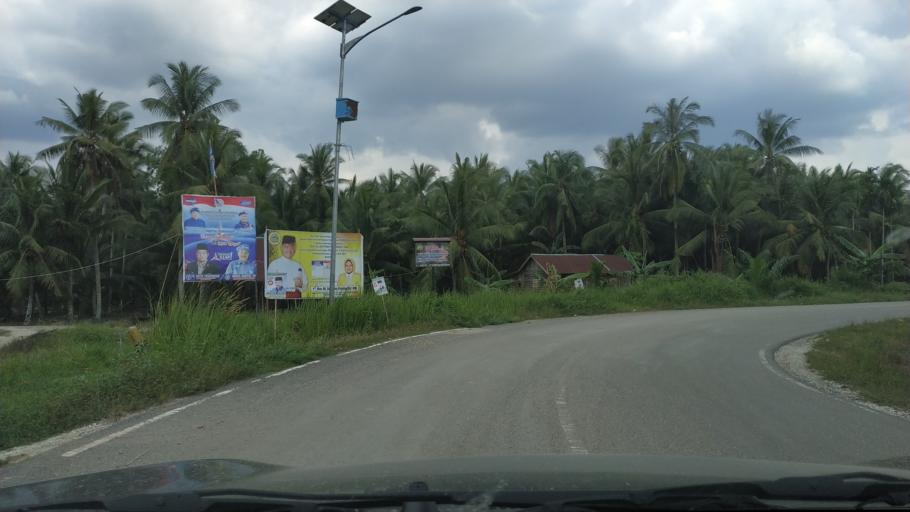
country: ID
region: Riau
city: Sungaisalak
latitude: -0.5629
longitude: 102.9658
